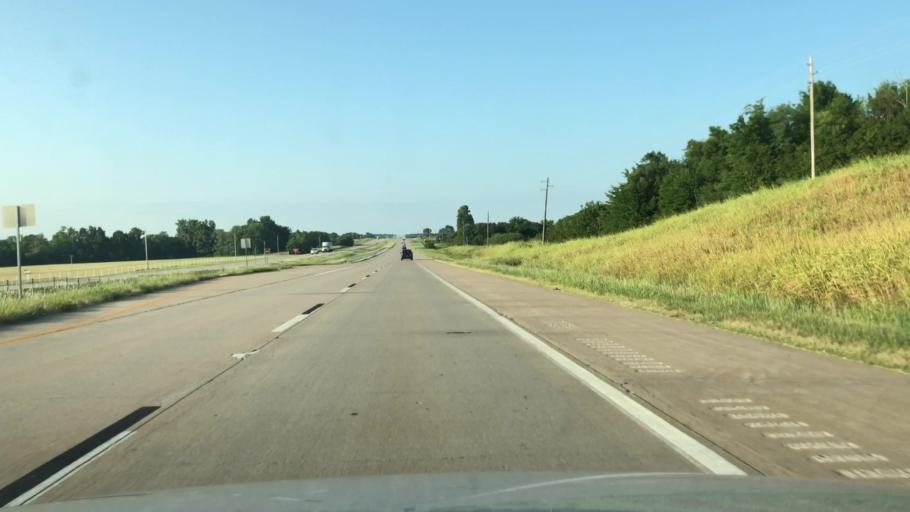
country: US
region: Oklahoma
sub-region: Osage County
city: Skiatook
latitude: 36.4744
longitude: -95.9208
